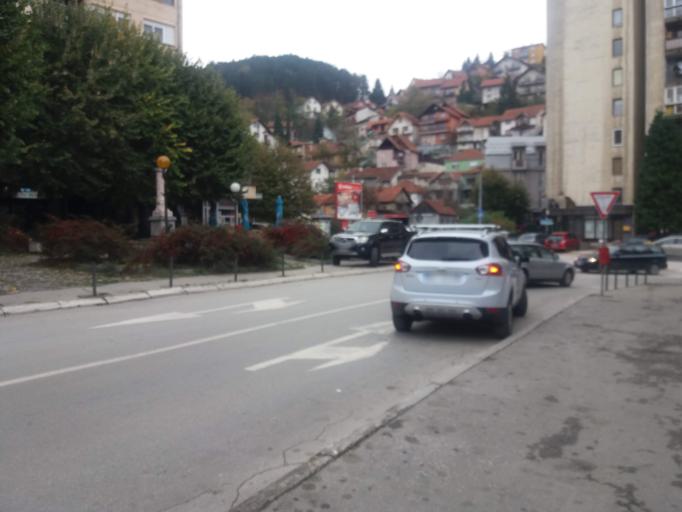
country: RS
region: Central Serbia
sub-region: Zlatiborski Okrug
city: Uzice
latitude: 43.8574
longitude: 19.8466
